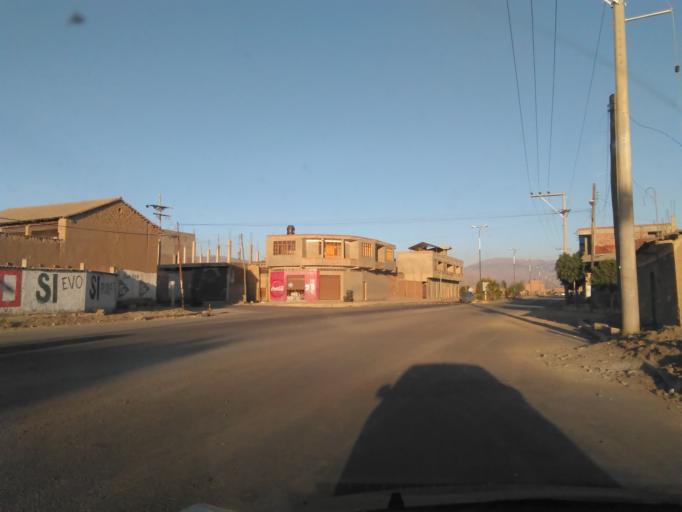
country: BO
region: Cochabamba
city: Punata
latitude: -17.5428
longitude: -65.8298
